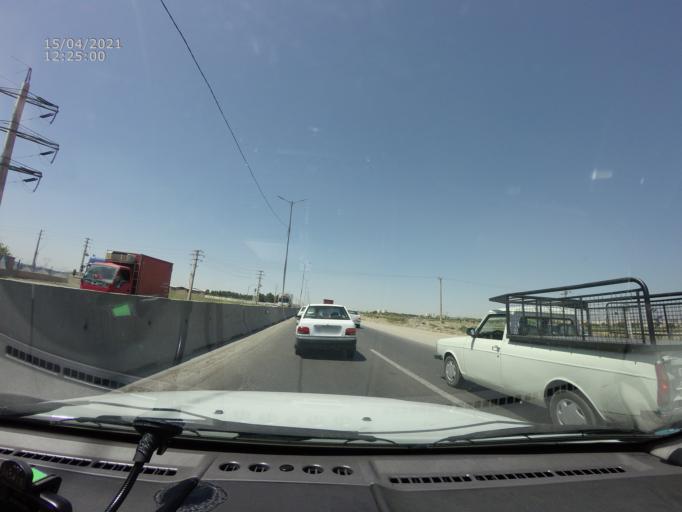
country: IR
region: Tehran
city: Eslamshahr
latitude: 35.5121
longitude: 51.2502
